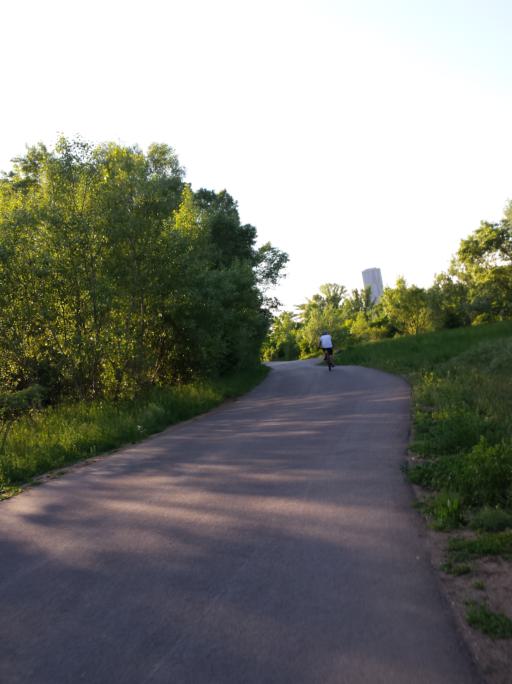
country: AT
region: Vienna
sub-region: Wien Stadt
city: Vienna
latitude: 48.2156
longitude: 16.4259
